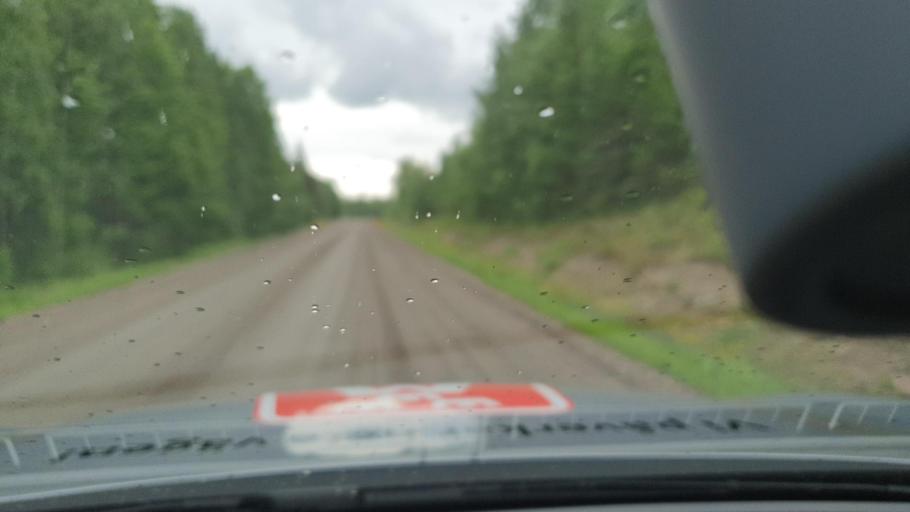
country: SE
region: Norrbotten
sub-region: Overtornea Kommun
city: OEvertornea
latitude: 66.4147
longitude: 23.5933
